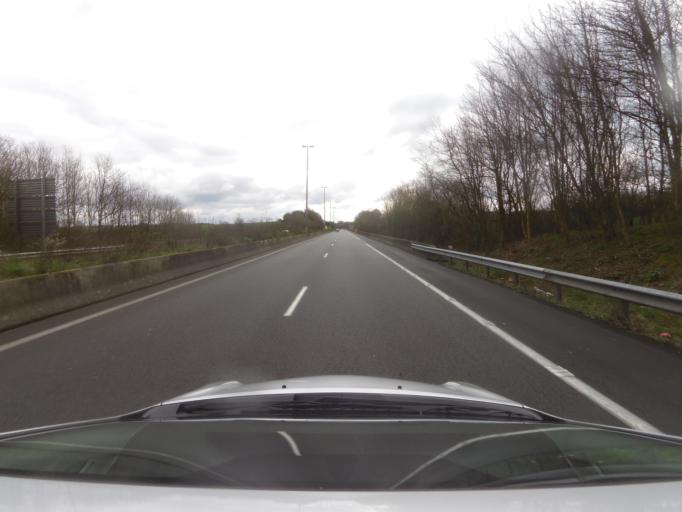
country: FR
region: Nord-Pas-de-Calais
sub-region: Departement du Pas-de-Calais
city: Saint-Martin-Boulogne
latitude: 50.7363
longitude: 1.6355
